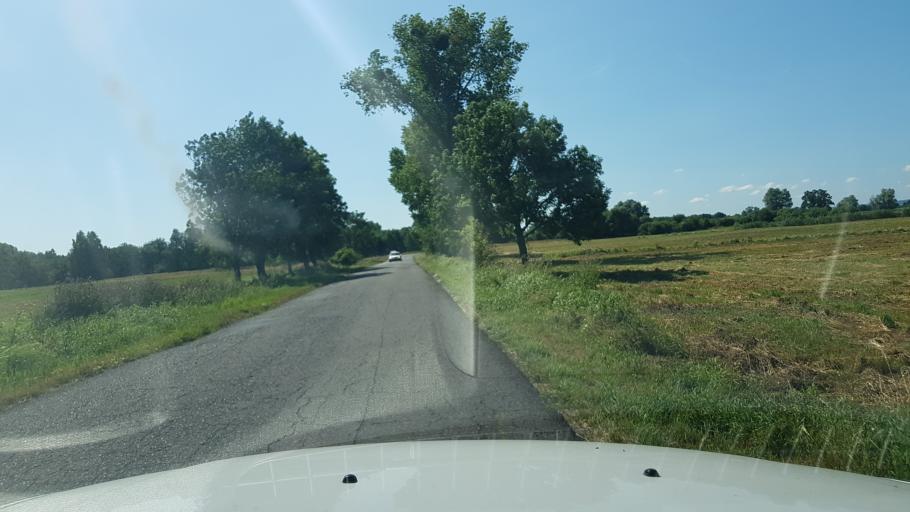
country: PL
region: West Pomeranian Voivodeship
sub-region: Powiat goleniowski
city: Goleniow
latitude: 53.4767
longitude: 14.7132
